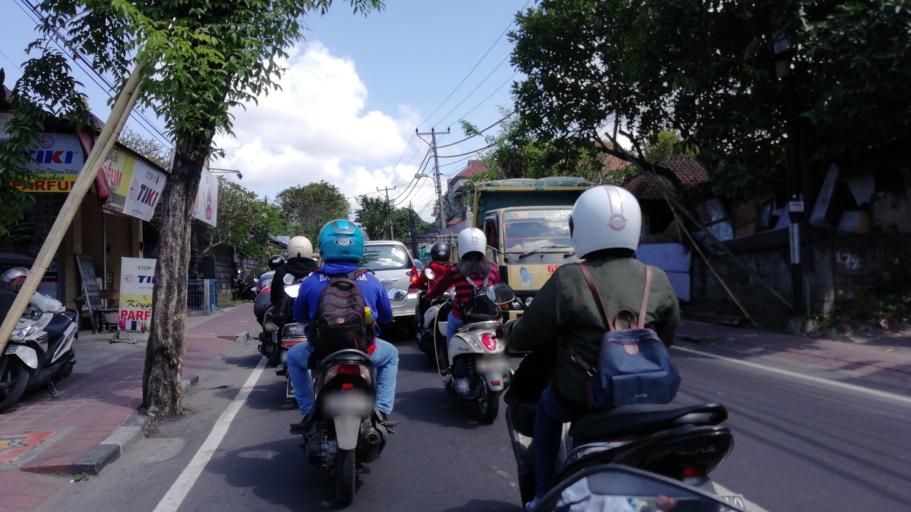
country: ID
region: Bali
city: Banjar Gunungpande
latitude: -8.6460
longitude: 115.1639
